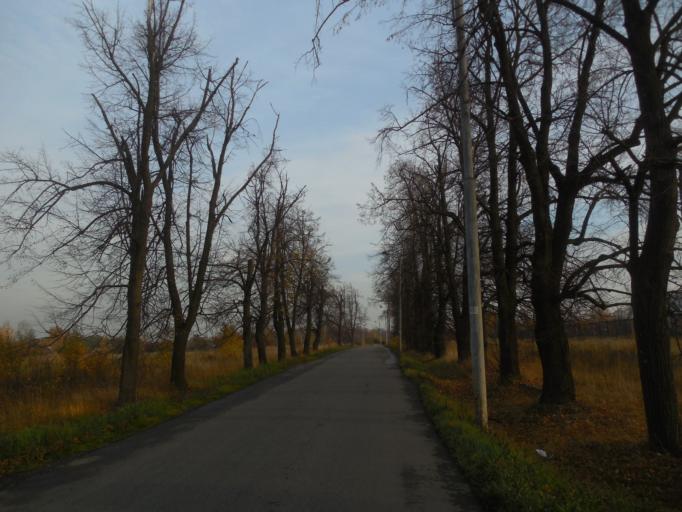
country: RU
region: Moskovskaya
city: Shcherbinka
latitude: 55.4983
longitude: 37.5793
